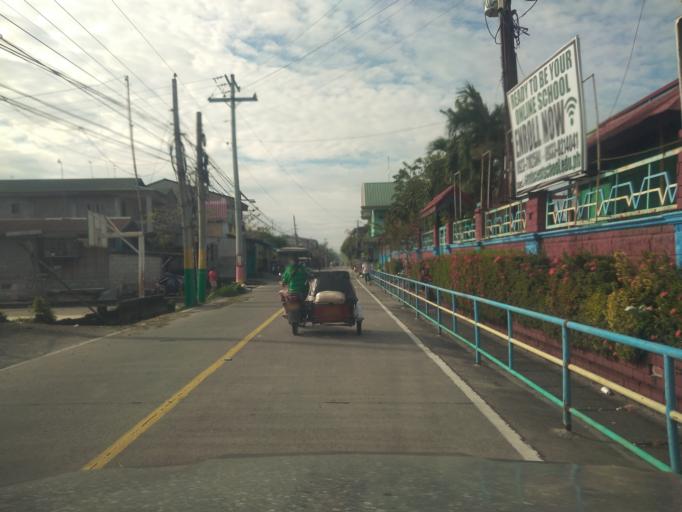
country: PH
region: Central Luzon
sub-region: Province of Pampanga
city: Sexmoan
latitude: 14.9471
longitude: 120.6232
